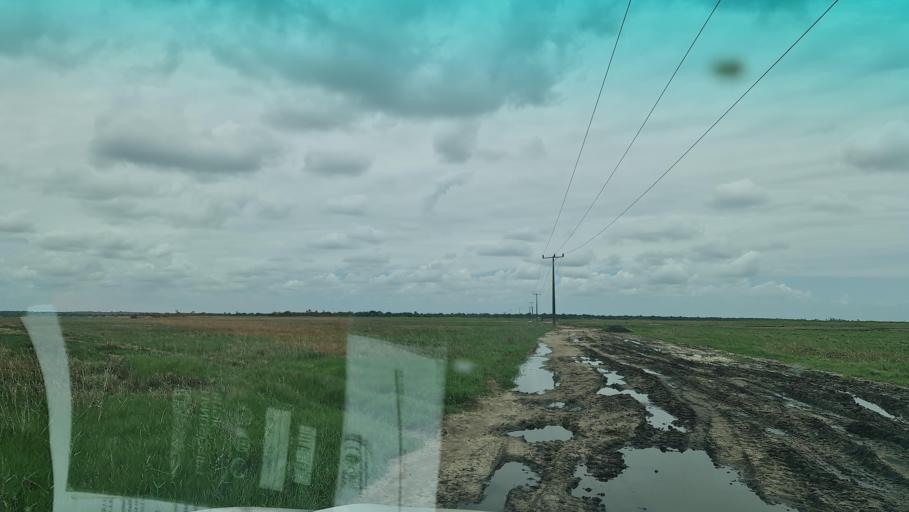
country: MZ
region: Maputo City
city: Maputo
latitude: -25.7148
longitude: 32.7022
